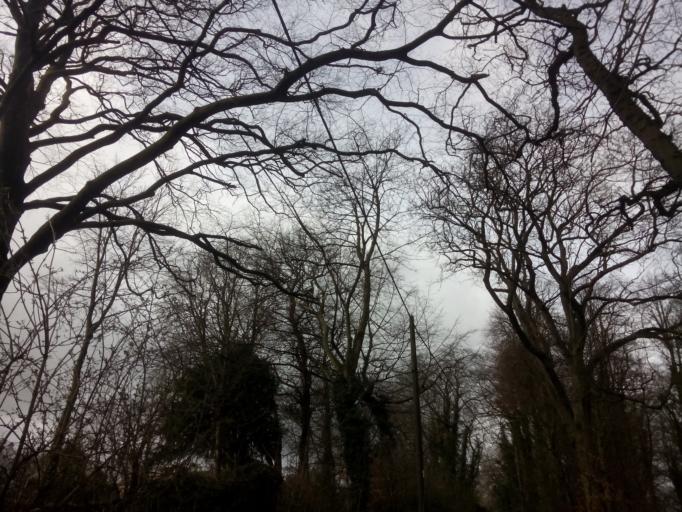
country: GB
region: England
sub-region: County Durham
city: Durham
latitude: 54.7606
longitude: -1.5836
